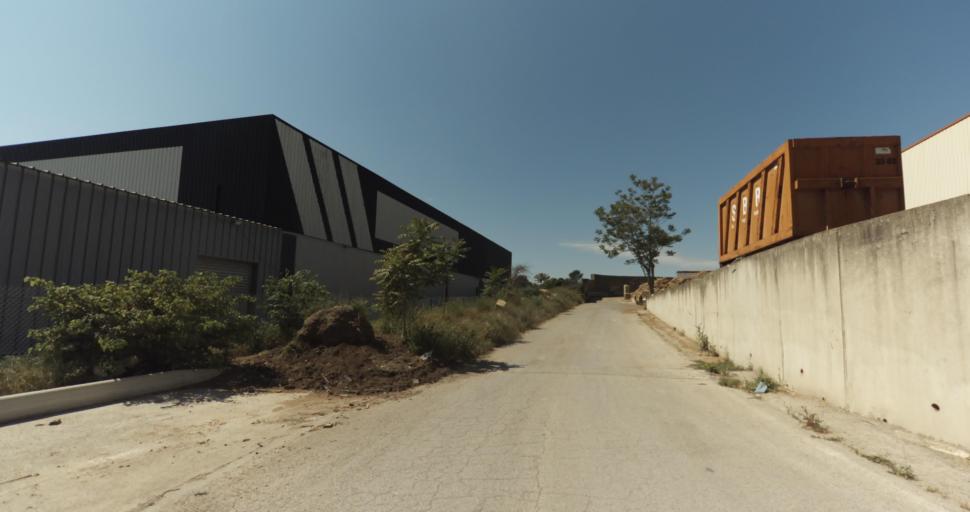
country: FR
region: Languedoc-Roussillon
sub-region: Departement du Gard
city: Milhaud
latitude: 43.8065
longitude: 4.3123
